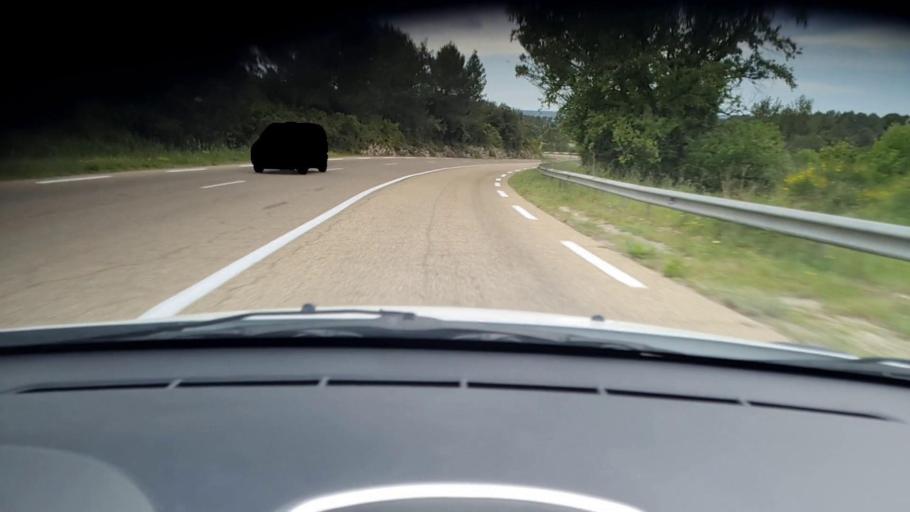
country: FR
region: Languedoc-Roussillon
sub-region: Departement du Gard
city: Nimes
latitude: 43.8700
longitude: 4.3768
